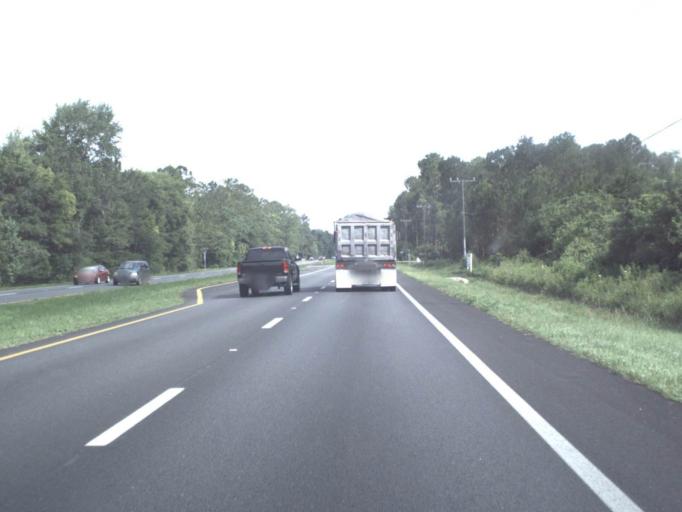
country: US
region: Florida
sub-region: Nassau County
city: Nassau Village-Ratliff
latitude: 30.5191
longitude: -81.7977
